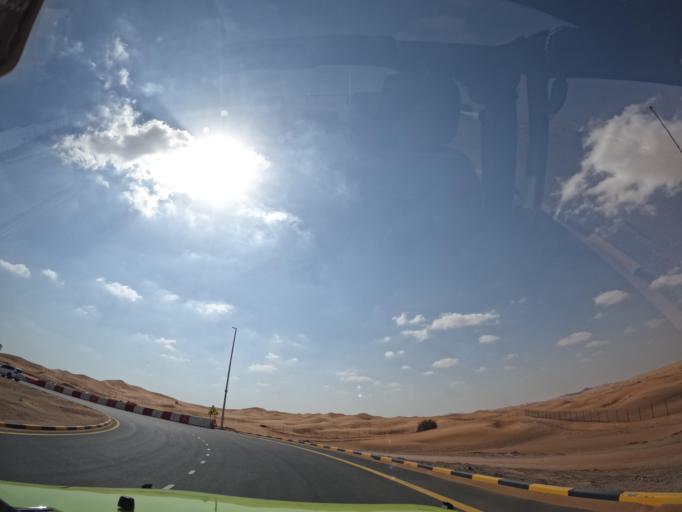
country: AE
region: Ash Shariqah
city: Adh Dhayd
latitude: 24.9407
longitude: 55.7313
